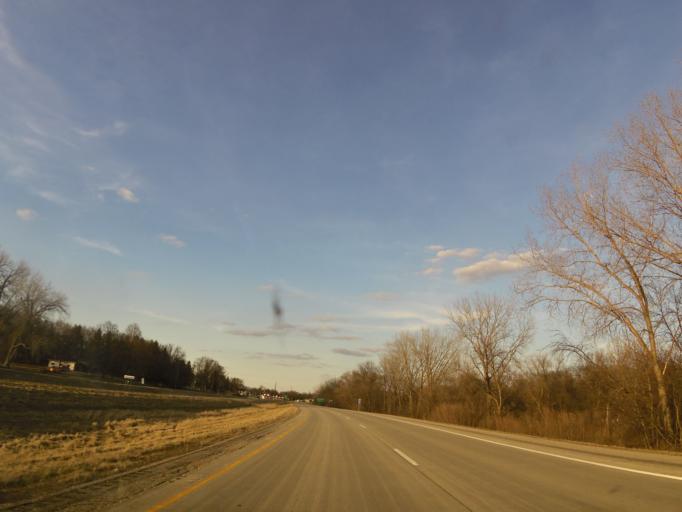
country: US
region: Minnesota
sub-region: McLeod County
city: Glencoe
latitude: 44.7581
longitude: -94.1637
